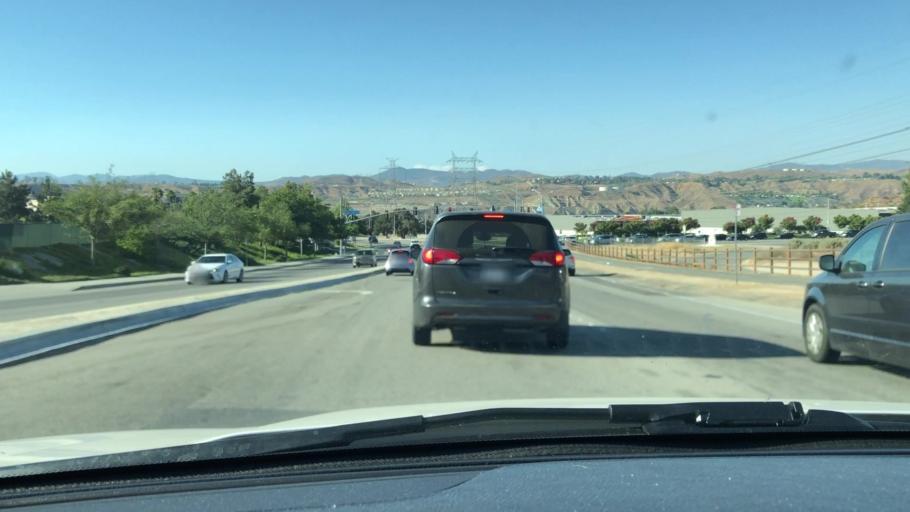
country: US
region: California
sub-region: Los Angeles County
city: Santa Clarita
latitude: 34.4113
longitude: -118.5026
